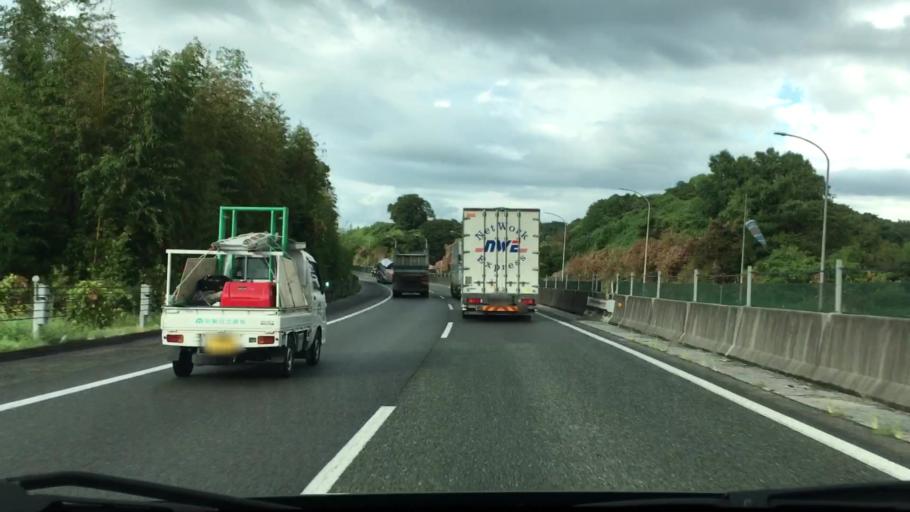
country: JP
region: Fukuoka
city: Nishifukuma
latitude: 33.7438
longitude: 130.5255
